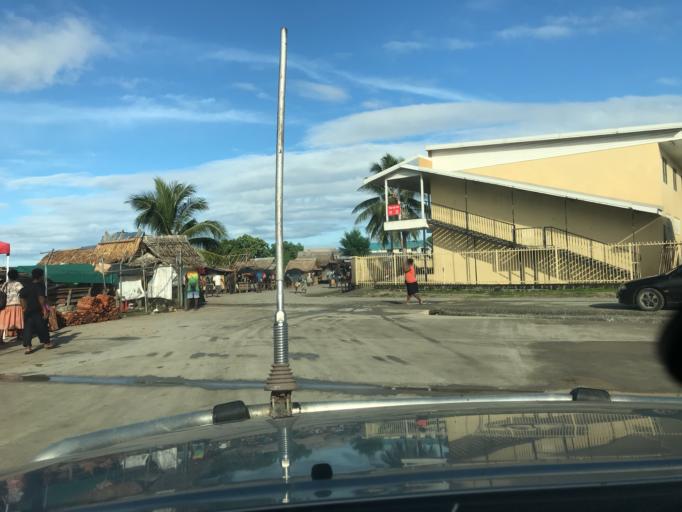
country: SB
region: Malaita
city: Auki
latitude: -8.7730
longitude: 160.6991
